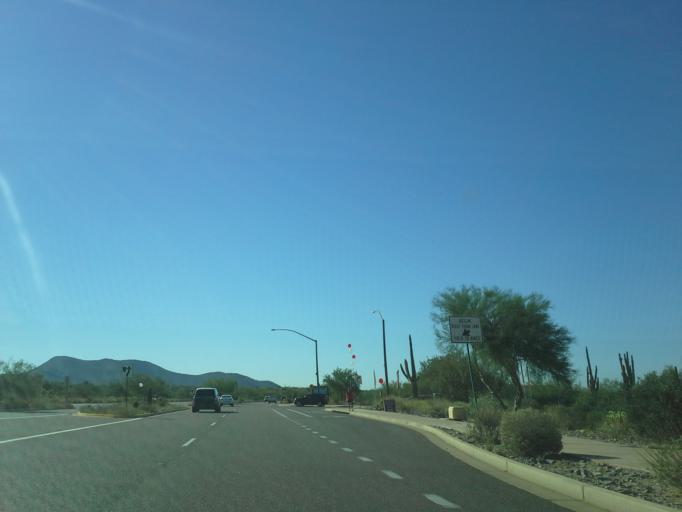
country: US
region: Arizona
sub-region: Maricopa County
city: Paradise Valley
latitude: 33.6486
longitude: -111.8631
